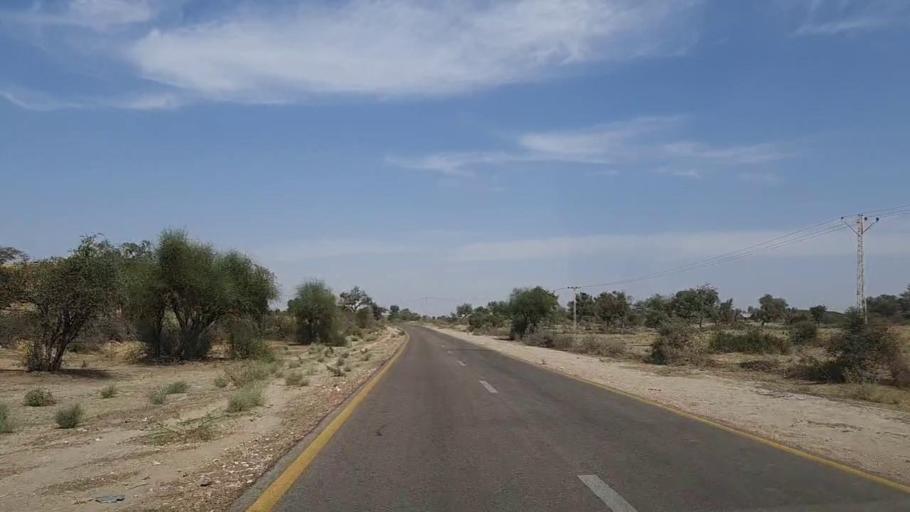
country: PK
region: Sindh
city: Mithi
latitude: 24.7927
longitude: 69.8143
